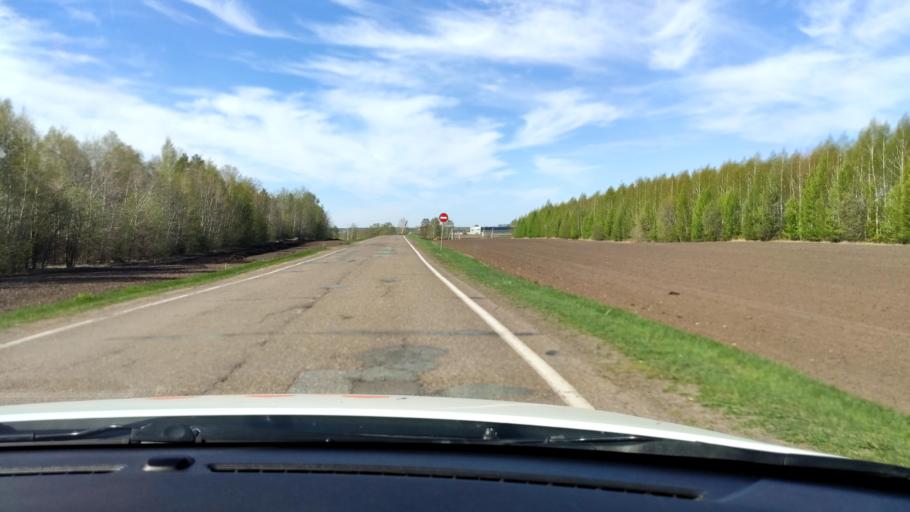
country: RU
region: Tatarstan
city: Stolbishchi
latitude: 55.5360
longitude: 49.2105
